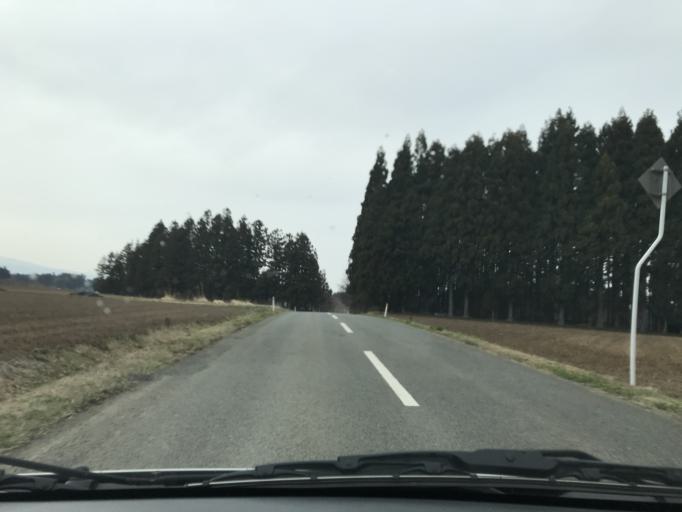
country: JP
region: Iwate
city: Mizusawa
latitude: 39.0917
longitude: 141.0691
